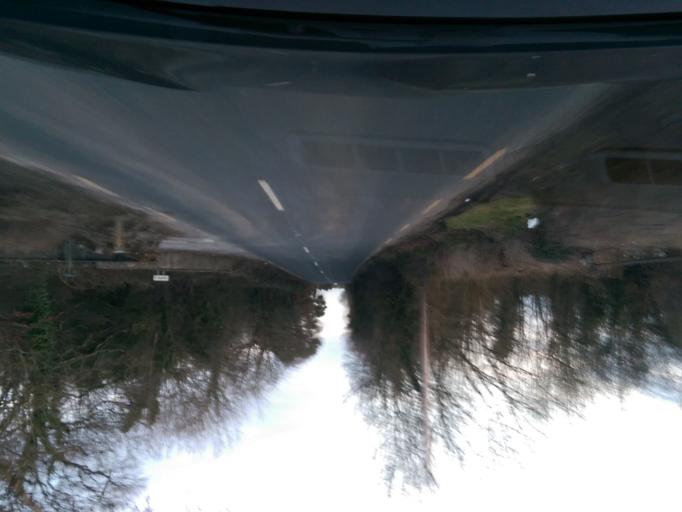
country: IE
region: Connaught
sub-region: County Galway
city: Portumna
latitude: 53.0391
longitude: -8.1144
